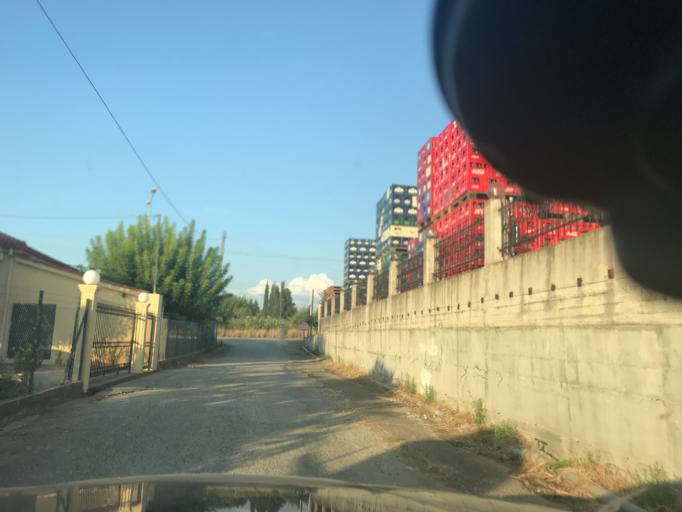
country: GR
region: West Greece
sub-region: Nomos Ileias
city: Pyrgos
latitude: 37.7042
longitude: 21.3898
